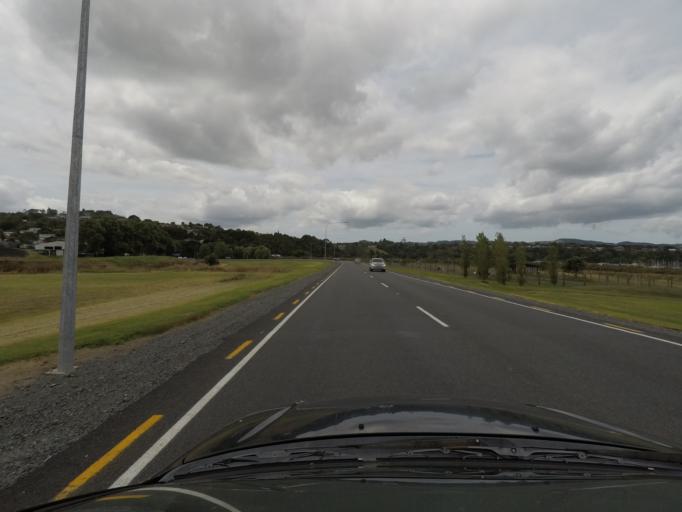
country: NZ
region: Northland
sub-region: Whangarei
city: Whangarei
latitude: -35.7346
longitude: 174.3414
